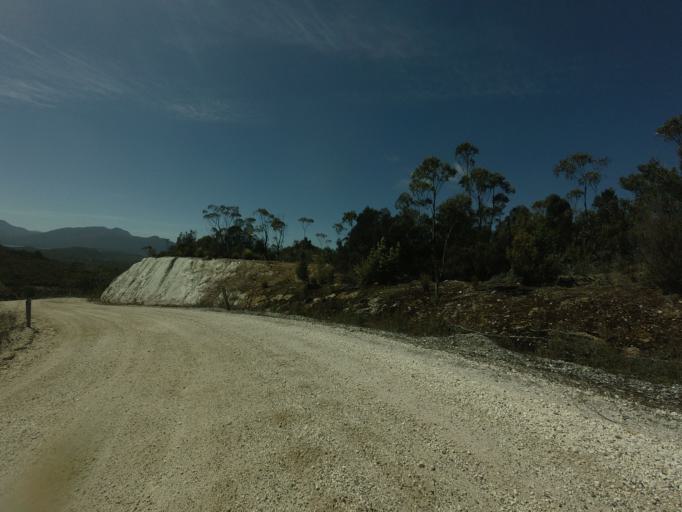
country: AU
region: Tasmania
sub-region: Huon Valley
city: Geeveston
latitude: -43.0410
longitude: 146.2752
